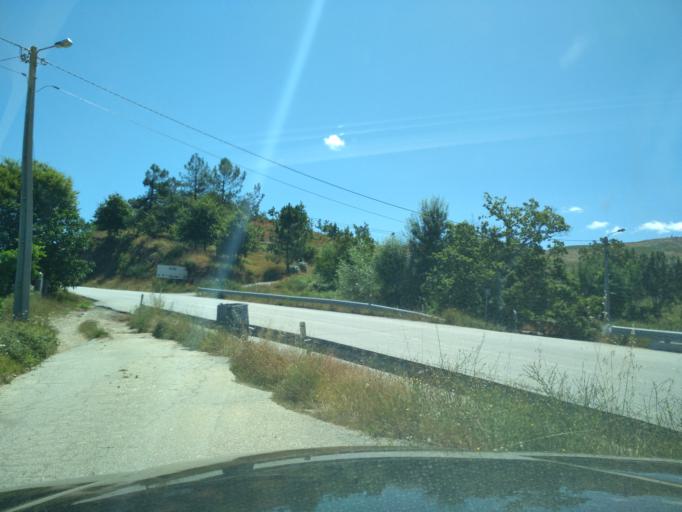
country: PT
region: Vila Real
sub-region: Ribeira de Pena
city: Ribeira de Pena
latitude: 41.5009
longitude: -7.7938
